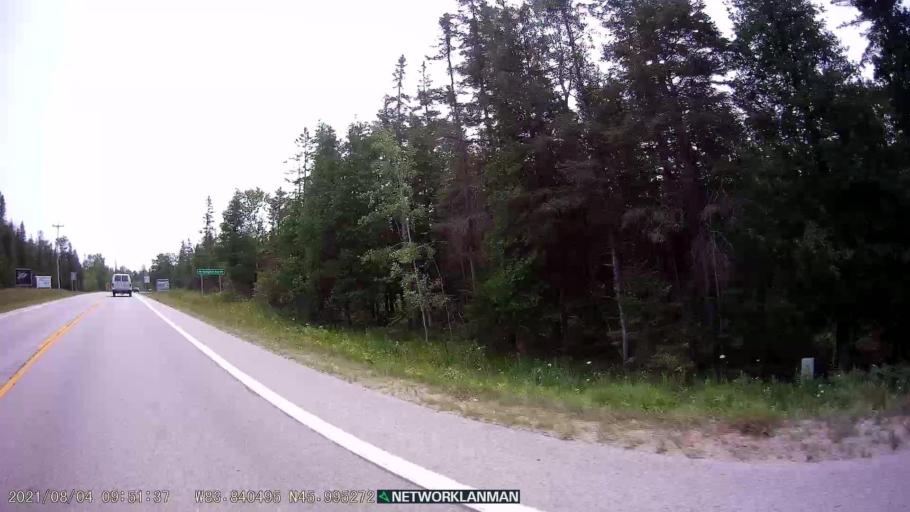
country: CA
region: Ontario
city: Thessalon
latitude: 45.9952
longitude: -83.8403
